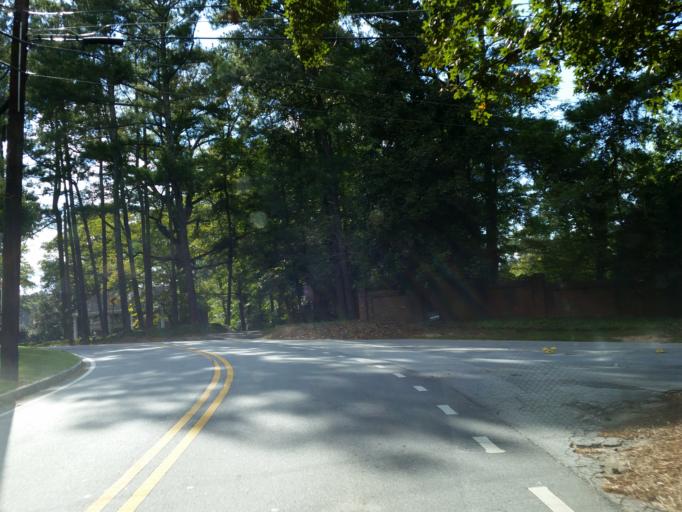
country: US
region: Georgia
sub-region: Cobb County
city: Vinings
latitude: 33.8702
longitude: -84.4266
